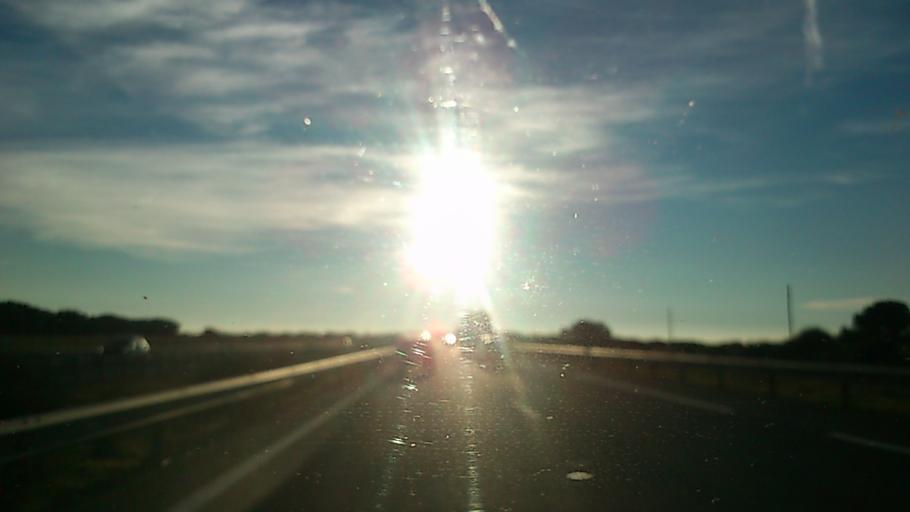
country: ES
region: Castille-La Mancha
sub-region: Provincia de Guadalajara
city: Utande
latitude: 40.8220
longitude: -2.9225
